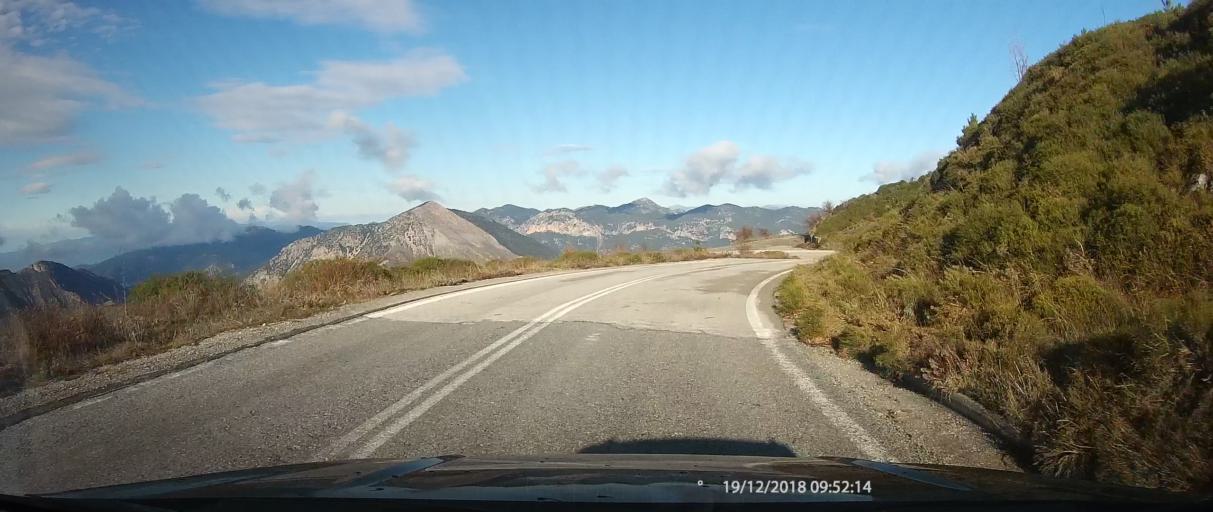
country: GR
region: Peloponnese
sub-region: Nomos Messinias
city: Paralia Vergas
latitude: 37.0739
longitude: 22.2550
